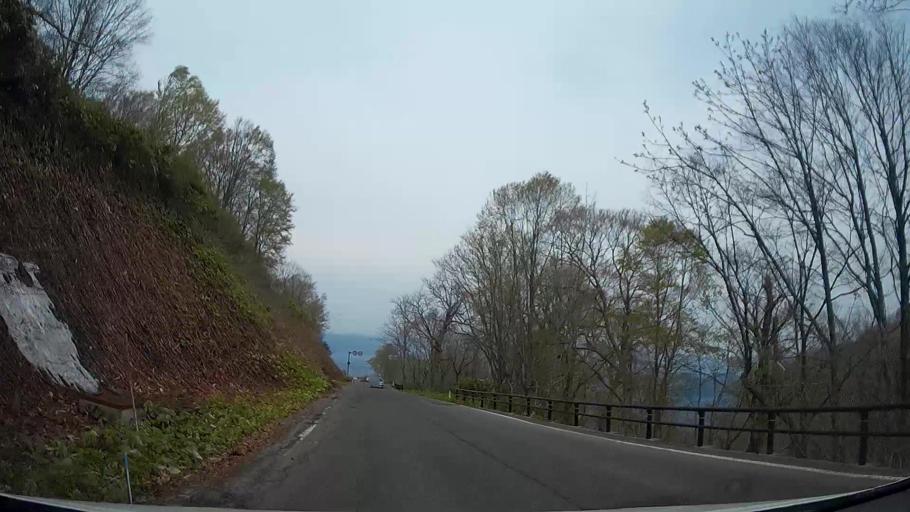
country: JP
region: Akita
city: Hanawa
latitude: 40.4068
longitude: 140.8652
